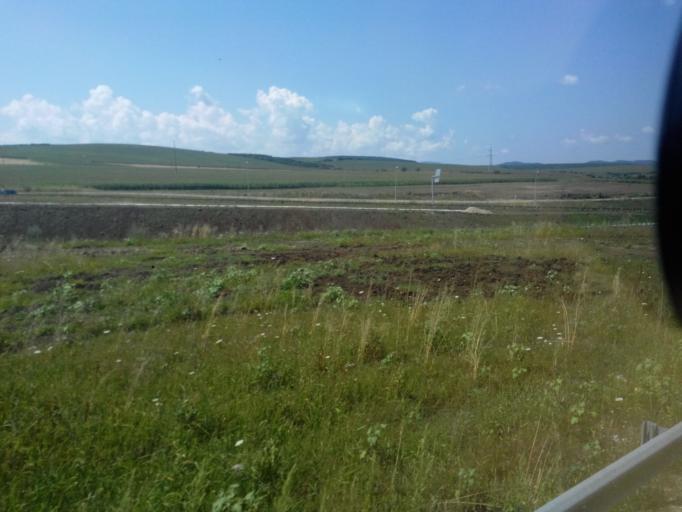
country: RO
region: Alba
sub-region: Comuna Garbova
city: Garbova
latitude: 45.9200
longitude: 23.7202
